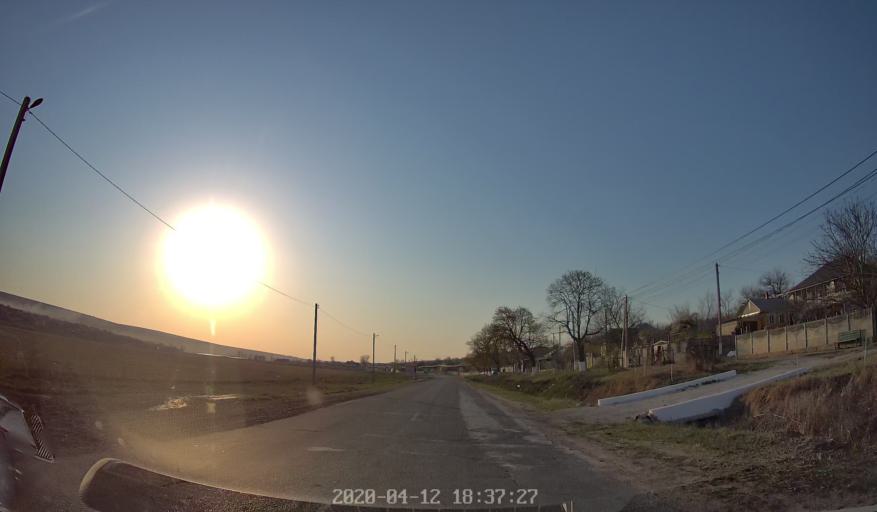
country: MD
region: Chisinau
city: Vadul lui Voda
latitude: 47.1212
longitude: 29.0152
